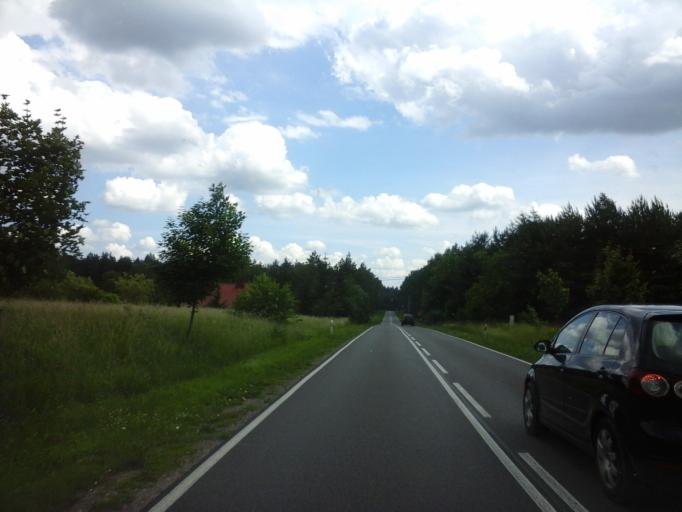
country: PL
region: West Pomeranian Voivodeship
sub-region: Powiat swidwinski
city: Slawoborze
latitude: 53.8817
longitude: 15.7228
